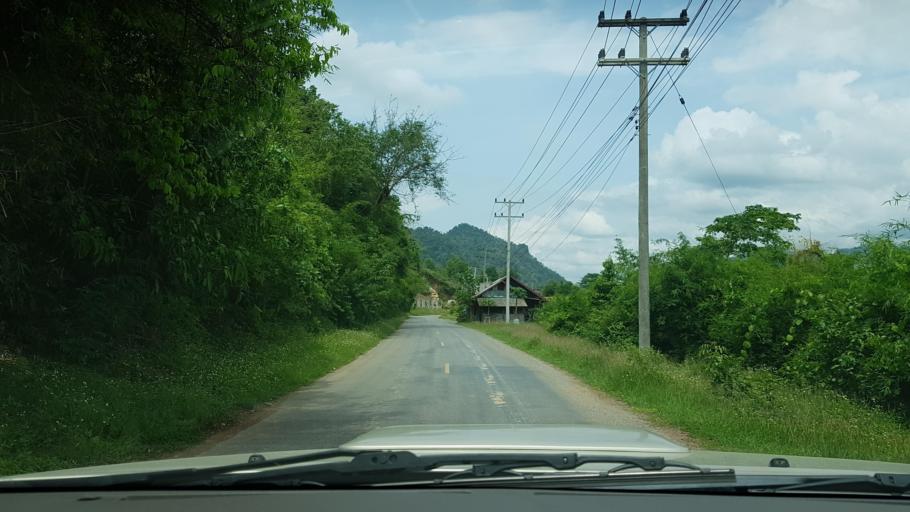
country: TH
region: Nan
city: Chaloem Phra Kiat
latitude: 19.9607
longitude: 101.2594
